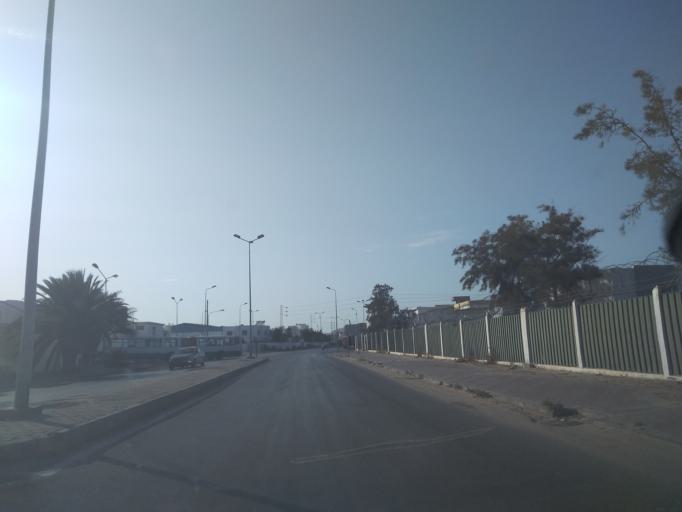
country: TN
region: Safaqis
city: Sfax
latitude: 34.7245
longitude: 10.7573
